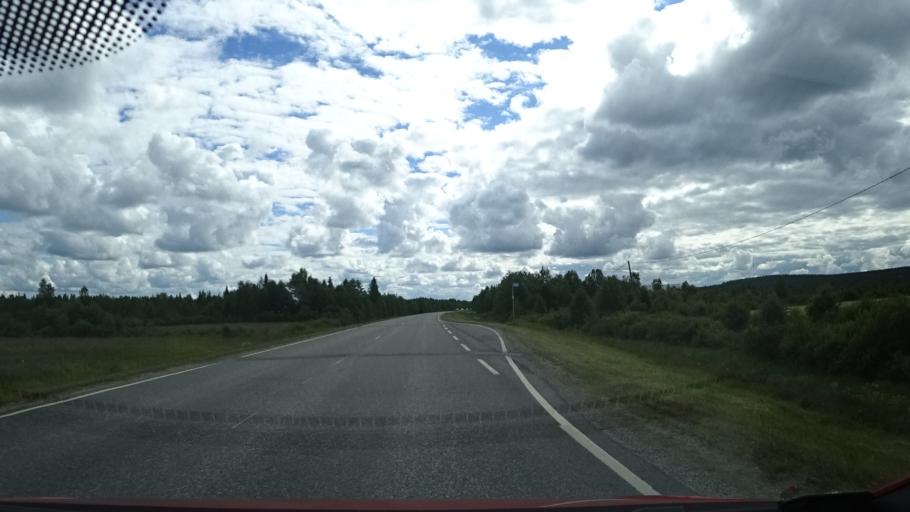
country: FI
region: Lapland
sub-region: Tunturi-Lappi
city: Kittilae
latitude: 67.6367
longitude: 24.9249
